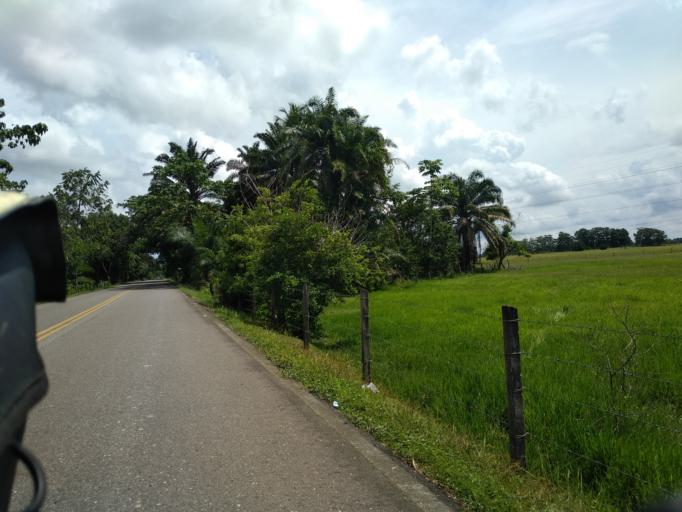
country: CO
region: Santander
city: Puerto Parra
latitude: 6.5047
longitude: -74.0597
